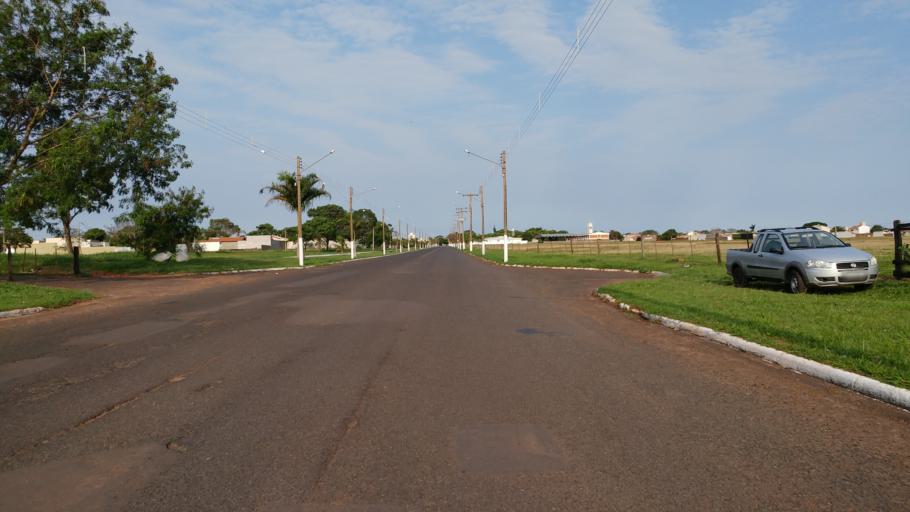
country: BR
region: Sao Paulo
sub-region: Paraguacu Paulista
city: Paraguacu Paulista
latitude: -22.4099
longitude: -50.5932
